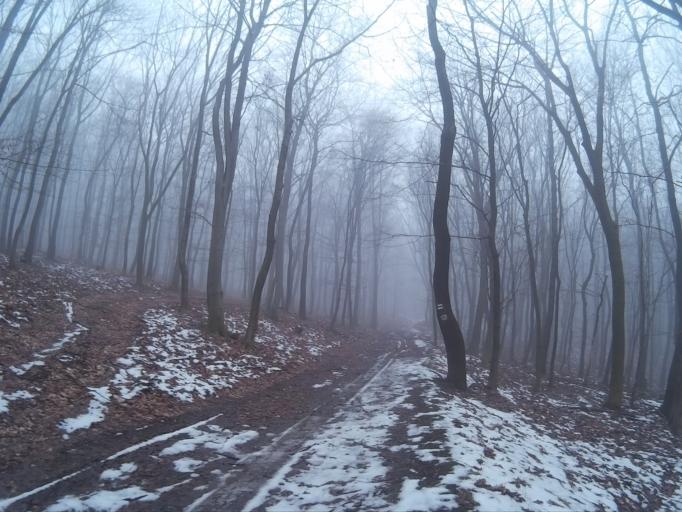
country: HU
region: Komarom-Esztergom
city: Tardos
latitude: 47.6829
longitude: 18.4735
